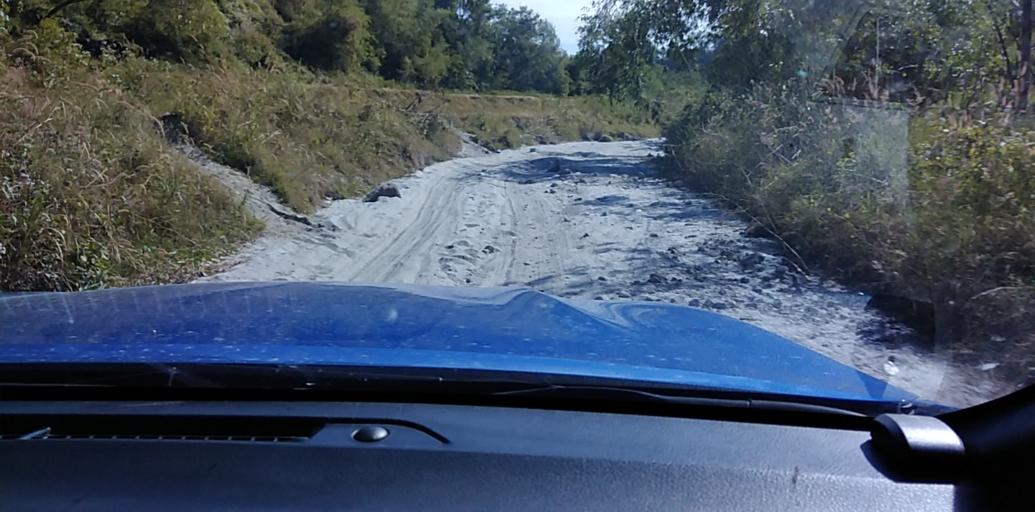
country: PH
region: Central Luzon
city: Santol
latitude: 15.1687
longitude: 120.4828
